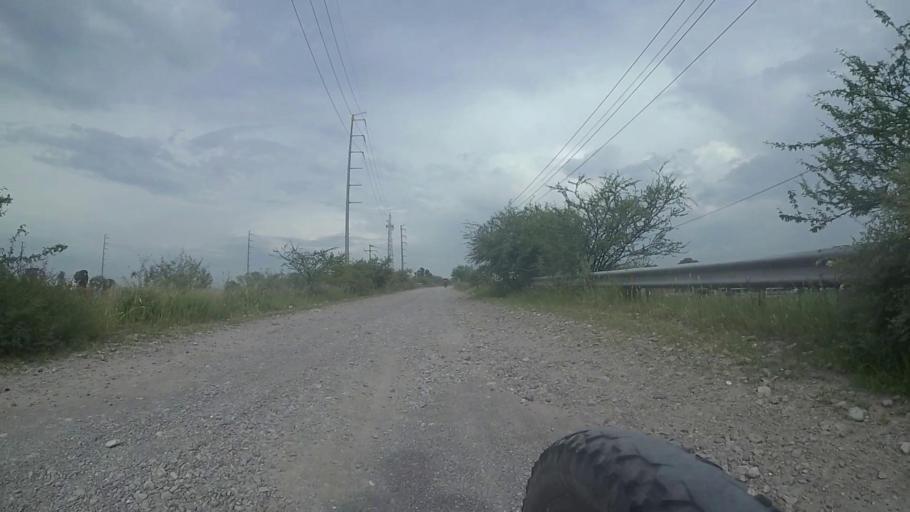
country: MX
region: Aguascalientes
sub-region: Aguascalientes
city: Penuelas (El Cienegal)
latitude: 21.7265
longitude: -102.2788
